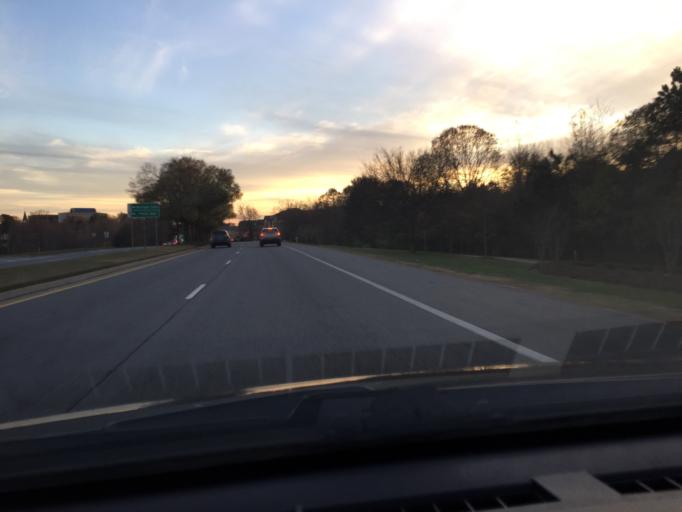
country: US
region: Georgia
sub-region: Fulton County
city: Johns Creek
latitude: 34.0595
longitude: -84.1733
